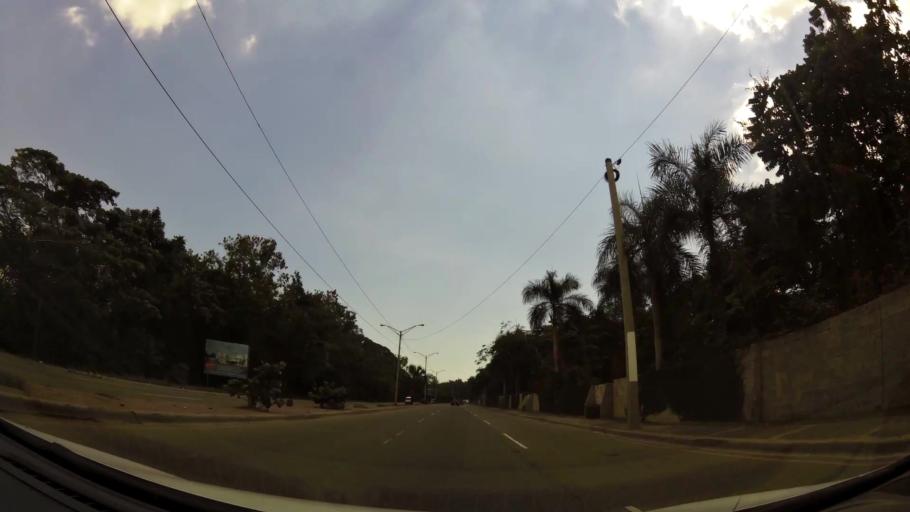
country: DO
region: Nacional
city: La Agustina
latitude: 18.5266
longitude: -69.9517
